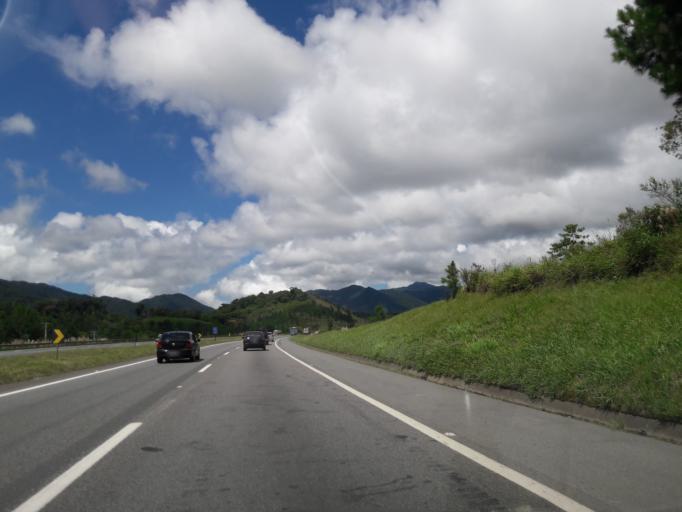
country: BR
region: Parana
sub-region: Antonina
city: Antonina
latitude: -25.0065
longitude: -48.5078
